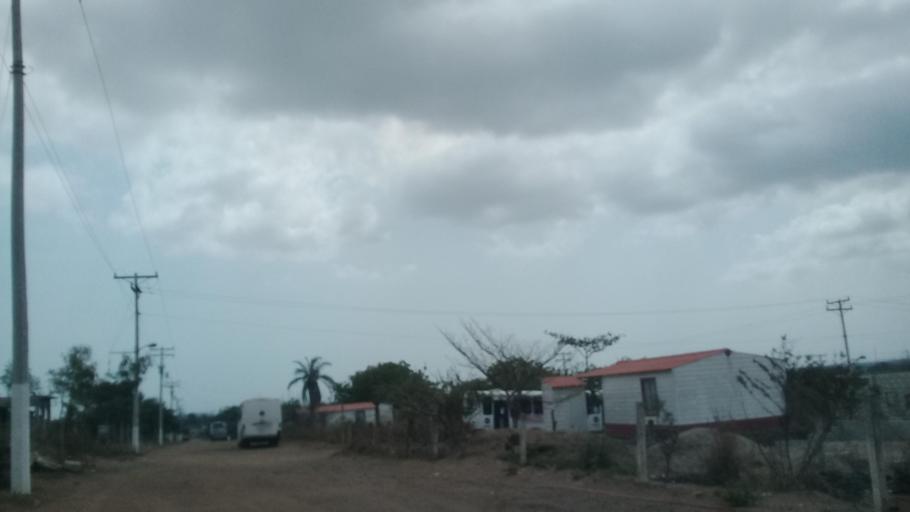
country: MX
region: Veracruz
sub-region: Veracruz
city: Las Amapolas
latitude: 19.1353
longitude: -96.2427
